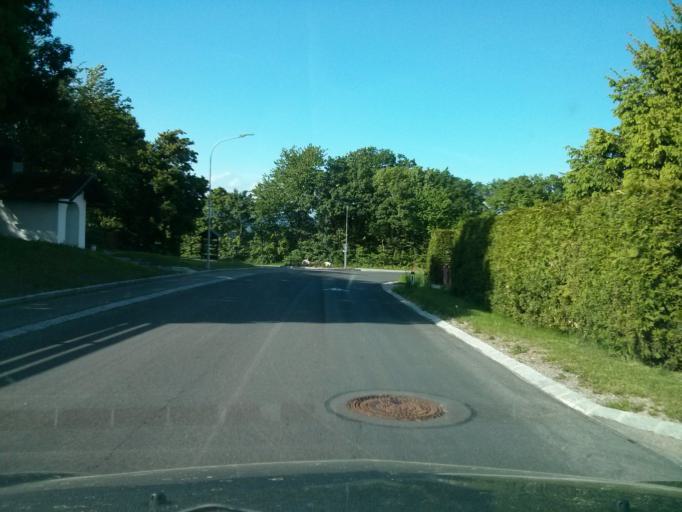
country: AT
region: Lower Austria
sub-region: Politischer Bezirk Baden
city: Hernstein
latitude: 47.9020
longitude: 16.1241
